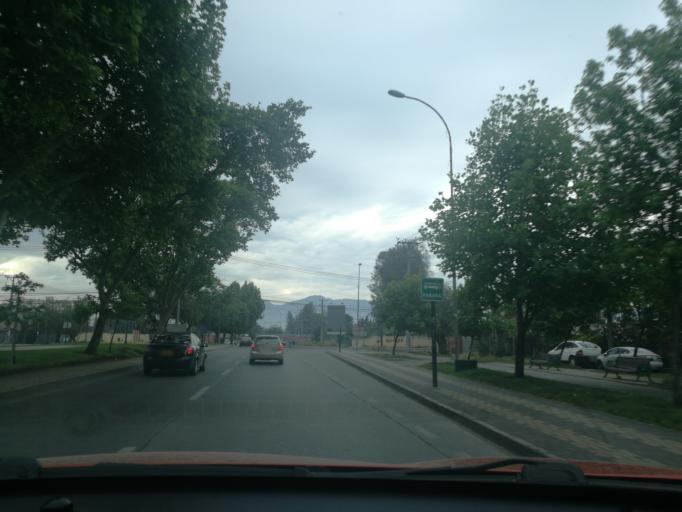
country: CL
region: O'Higgins
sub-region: Provincia de Cachapoal
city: Rancagua
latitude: -34.1676
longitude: -70.7245
